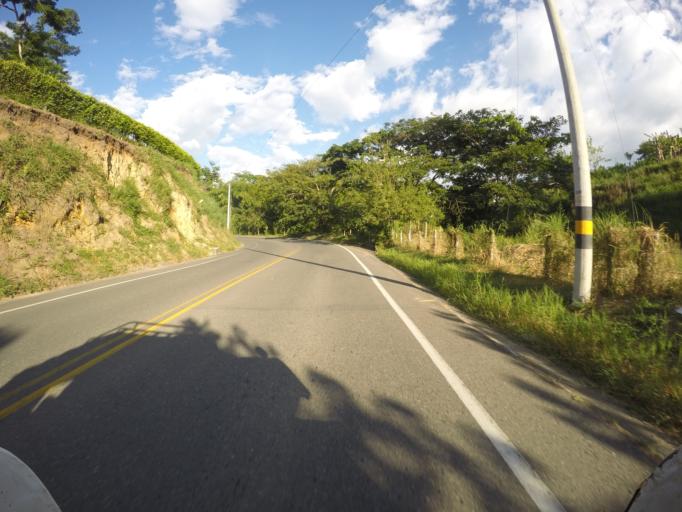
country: CO
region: Valle del Cauca
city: Alcala
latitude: 4.7006
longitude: -75.8325
